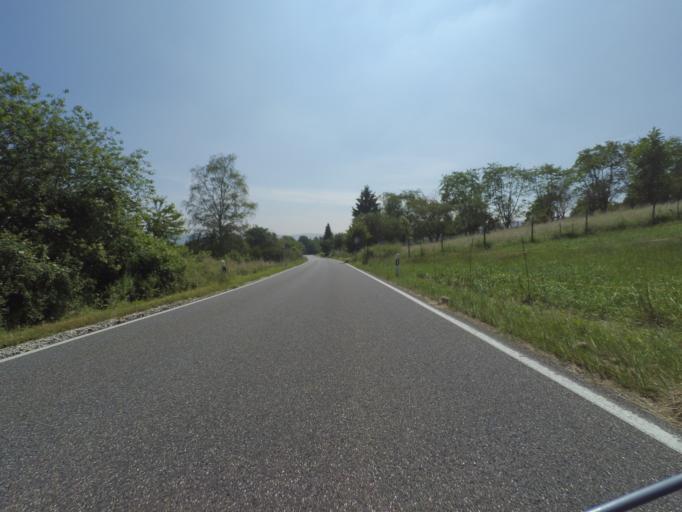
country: DE
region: Rheinland-Pfalz
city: Filsen
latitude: 50.2269
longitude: 7.5714
